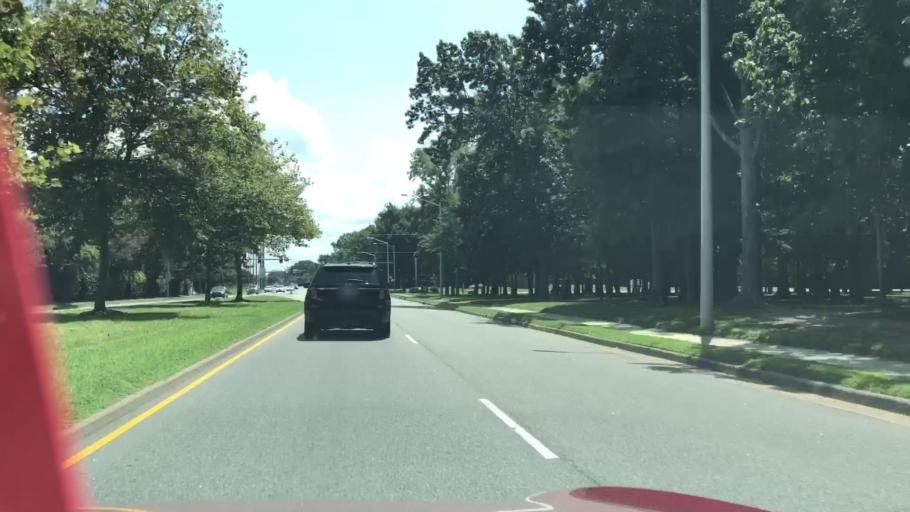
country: US
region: Virginia
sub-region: City of Virginia Beach
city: Virginia Beach
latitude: 36.8875
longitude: -76.0498
